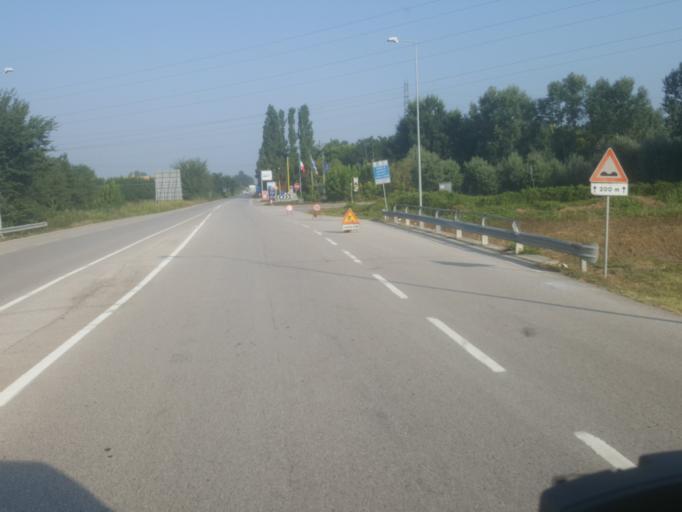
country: IT
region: Emilia-Romagna
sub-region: Provincia di Ravenna
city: Fornace Zarattini
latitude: 44.4292
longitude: 12.1534
